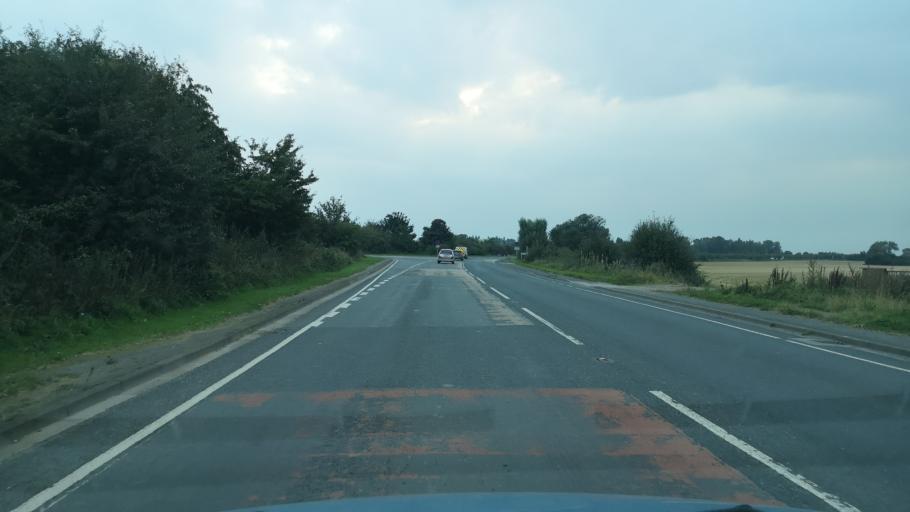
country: GB
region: England
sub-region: East Riding of Yorkshire
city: Pollington
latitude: 53.6834
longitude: -1.0543
